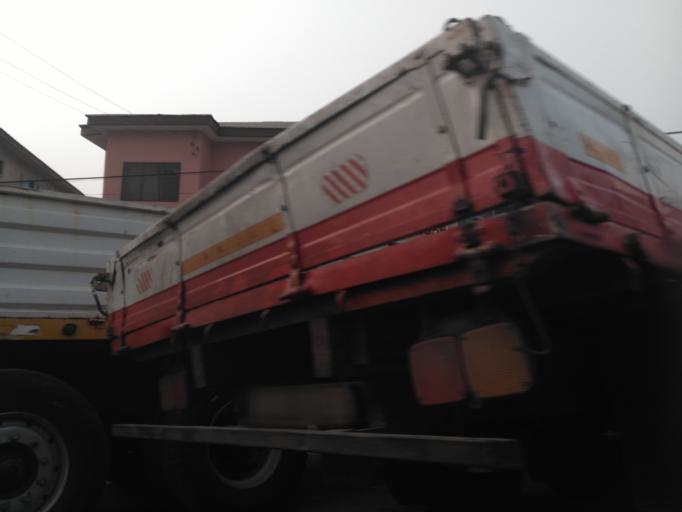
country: GH
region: Ashanti
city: Kumasi
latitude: 6.6895
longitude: -1.6208
